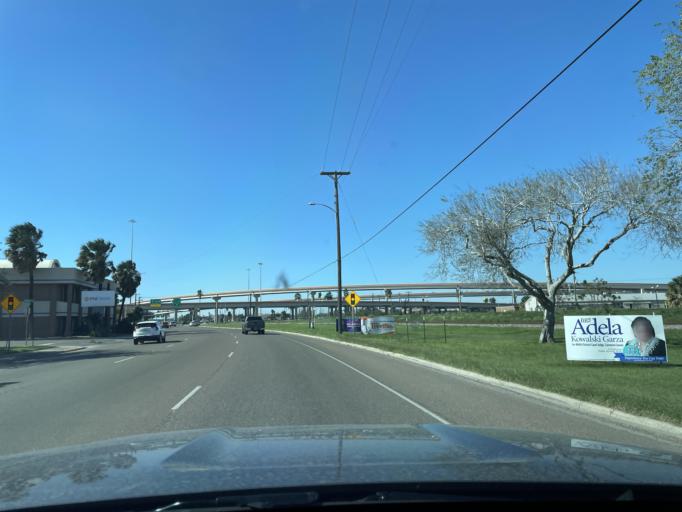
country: US
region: Texas
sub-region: Cameron County
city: Harlingen
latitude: 26.1907
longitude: -97.7156
